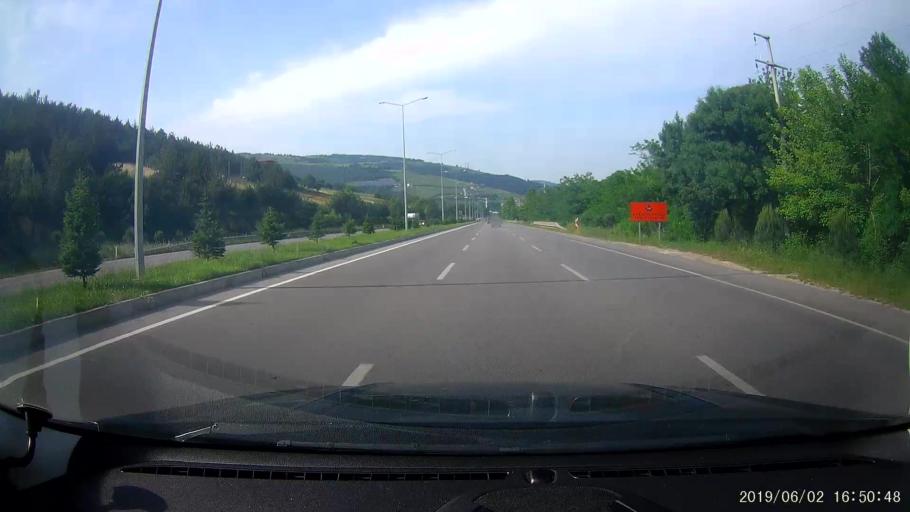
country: TR
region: Samsun
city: Taflan
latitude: 41.2625
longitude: 36.1757
